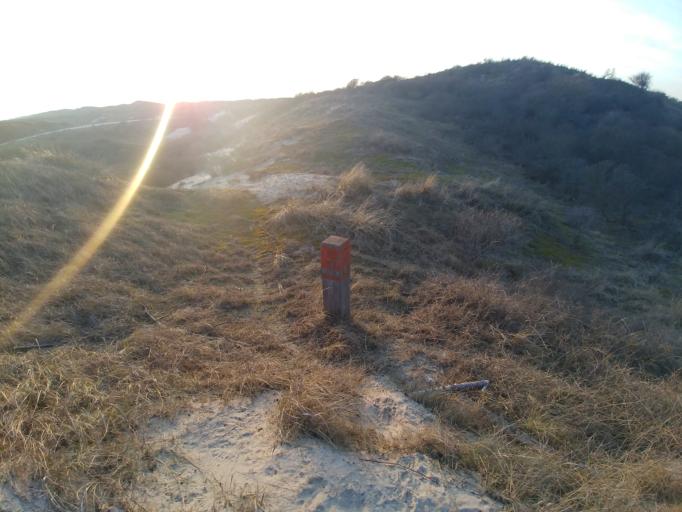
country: NL
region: South Holland
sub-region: Gemeente Wassenaar
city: Wassenaar
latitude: 52.1610
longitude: 4.3511
